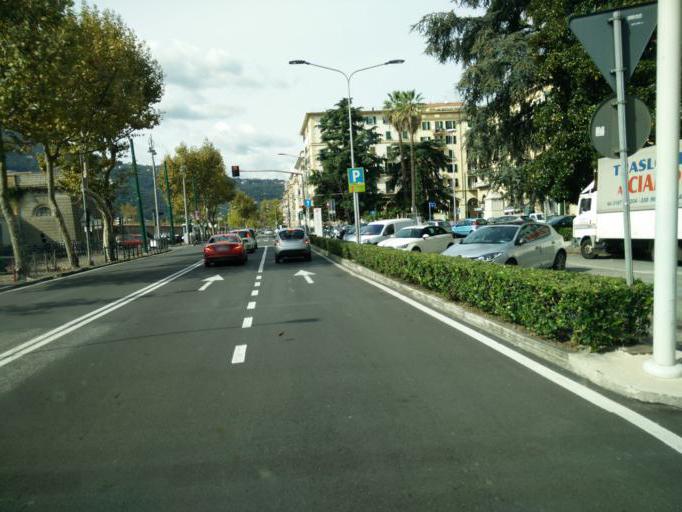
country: IT
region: Liguria
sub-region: Provincia di La Spezia
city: La Spezia
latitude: 44.1015
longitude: 9.8212
